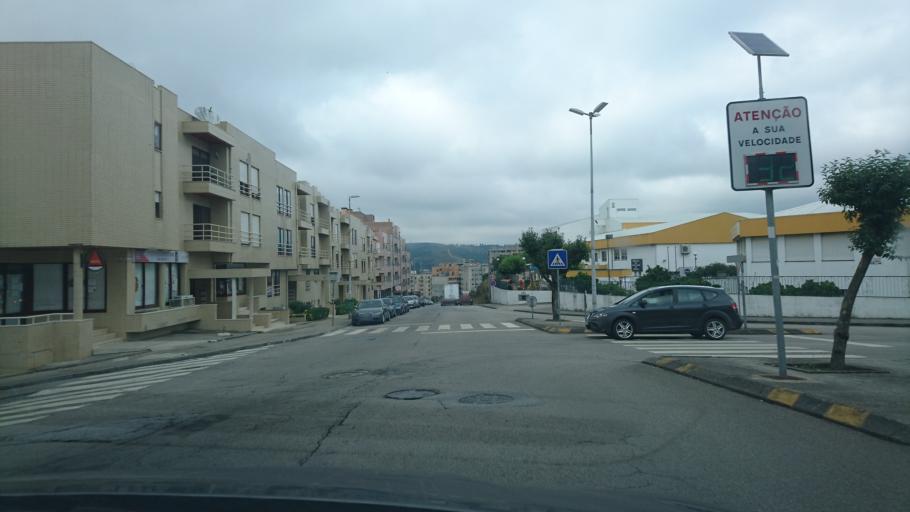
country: PT
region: Porto
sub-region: Valongo
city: Valongo
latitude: 41.1952
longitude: -8.5099
